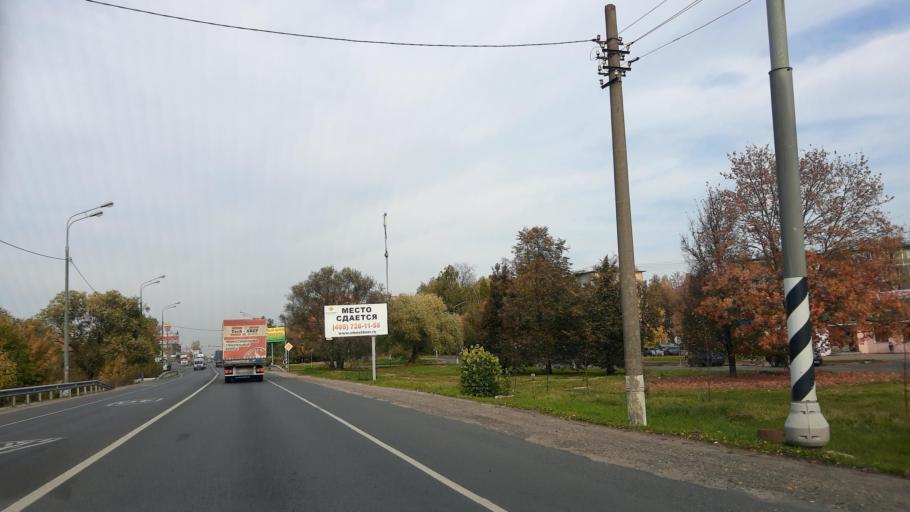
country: RU
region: Moskovskaya
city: Elektrostal'
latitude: 55.7656
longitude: 38.4355
